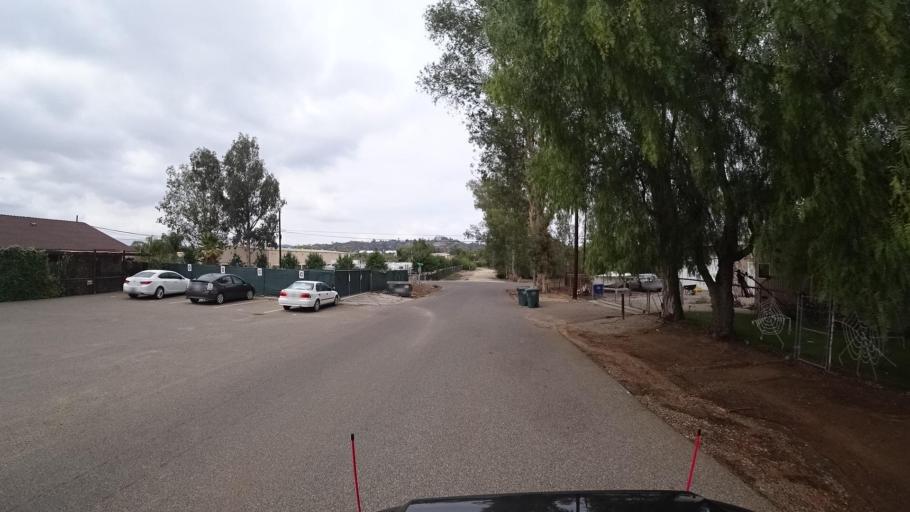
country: US
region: California
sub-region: San Diego County
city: Ramona
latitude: 33.0417
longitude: -116.8706
